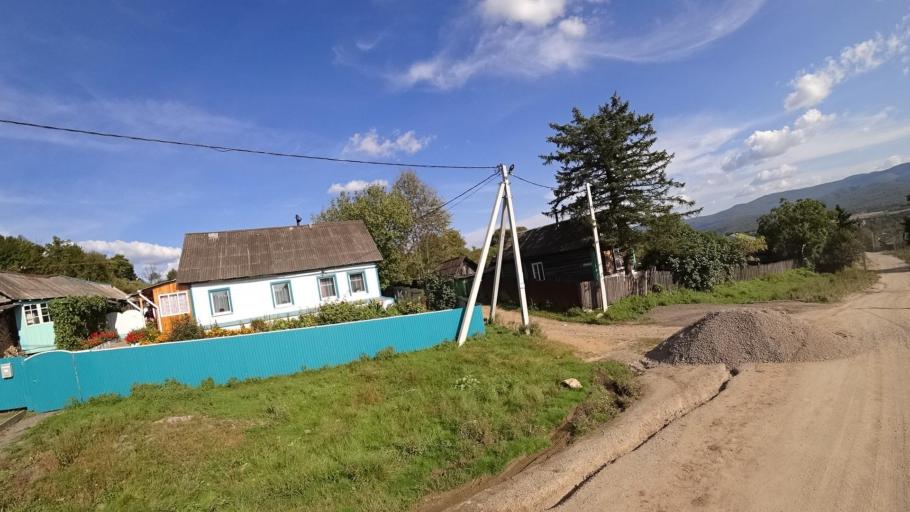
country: RU
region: Jewish Autonomous Oblast
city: Birakan
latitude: 48.9966
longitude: 131.7131
